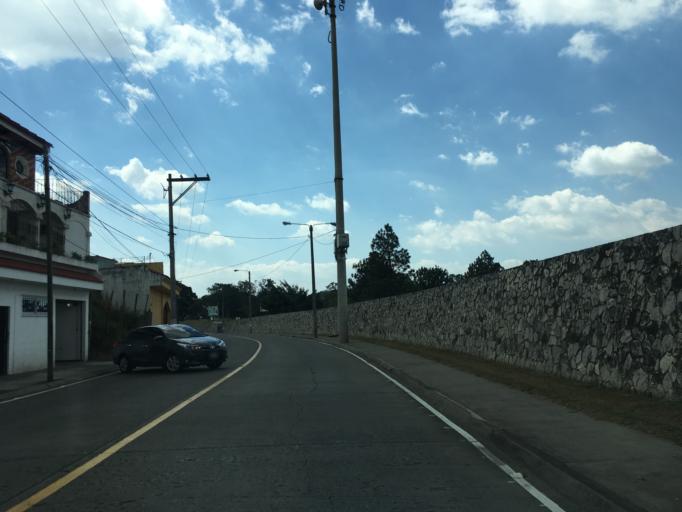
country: GT
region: Guatemala
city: Guatemala City
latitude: 14.6263
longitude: -90.4630
